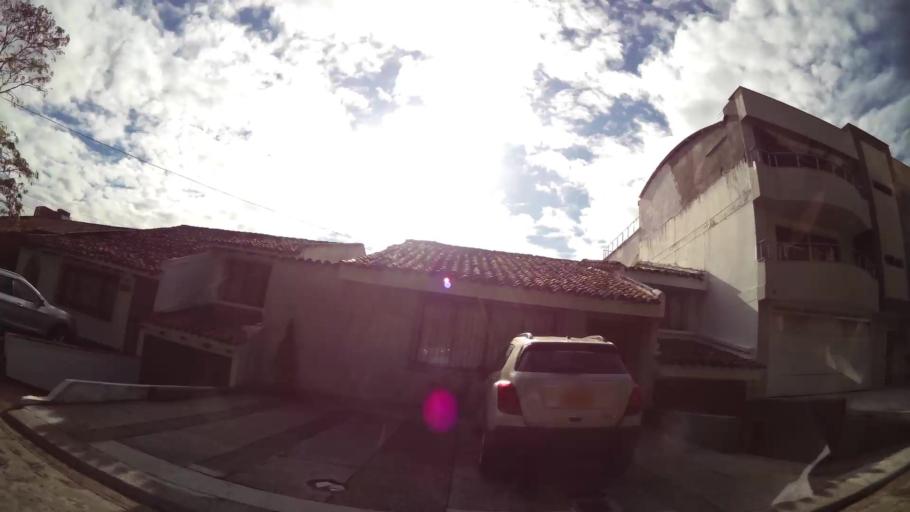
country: CO
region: Valle del Cauca
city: Cali
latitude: 3.4355
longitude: -76.5489
